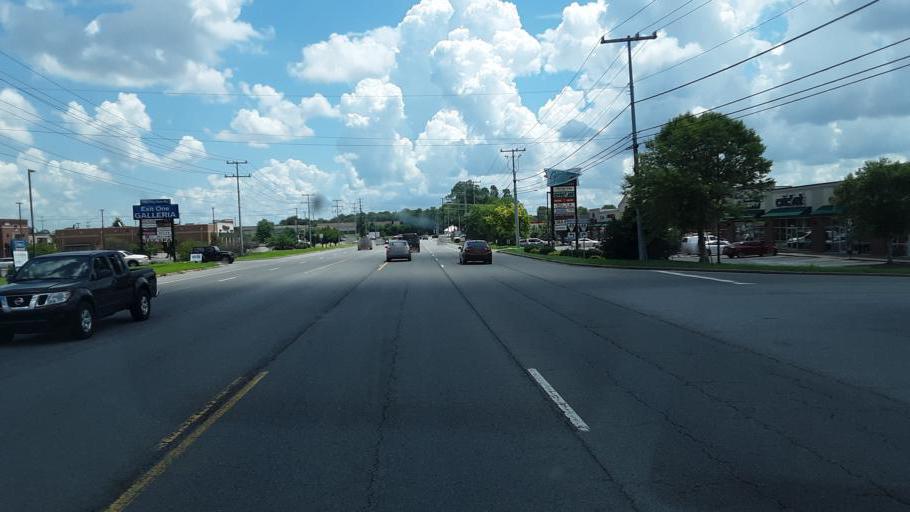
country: US
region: Tennessee
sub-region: Montgomery County
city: Clarksville
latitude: 36.6251
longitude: -87.3210
